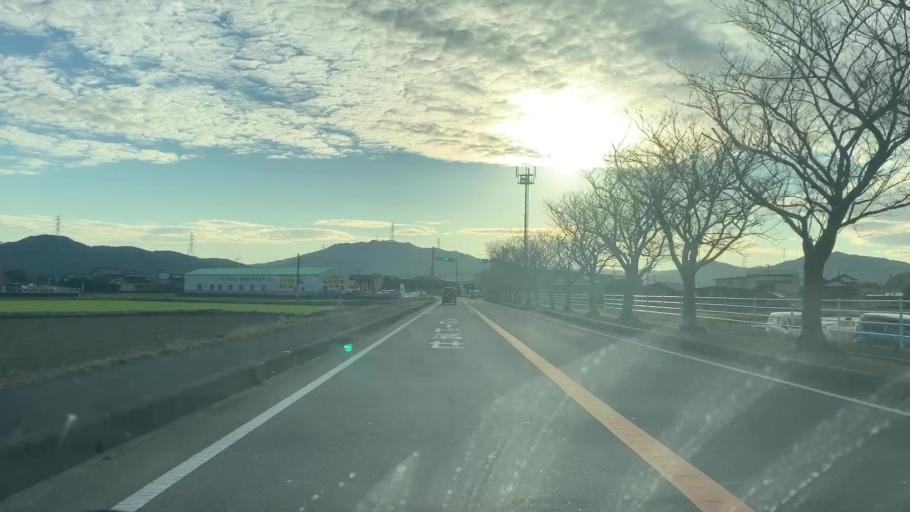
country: JP
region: Saga Prefecture
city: Karatsu
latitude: 33.4072
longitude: 129.9879
